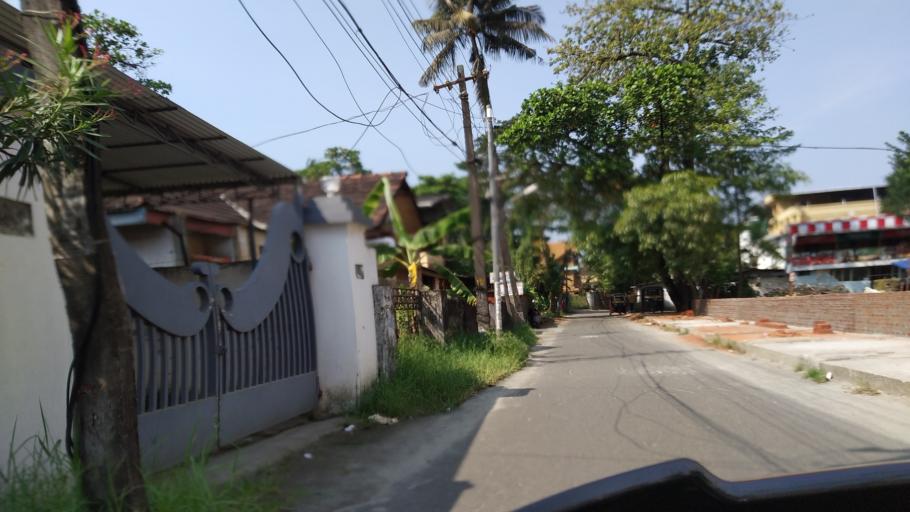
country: IN
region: Kerala
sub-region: Ernakulam
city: Cochin
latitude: 9.9730
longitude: 76.2894
